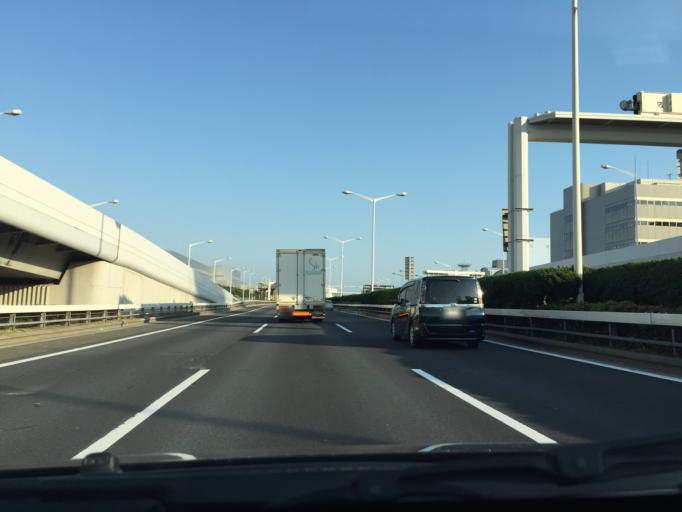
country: JP
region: Kanagawa
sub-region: Kawasaki-shi
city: Kawasaki
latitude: 35.5418
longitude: 139.7922
